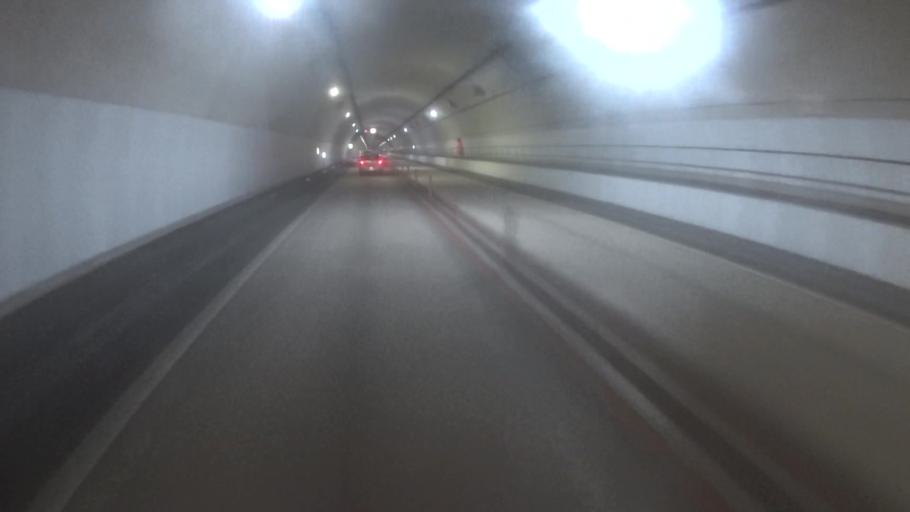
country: JP
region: Kyoto
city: Ayabe
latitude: 35.3280
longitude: 135.3135
